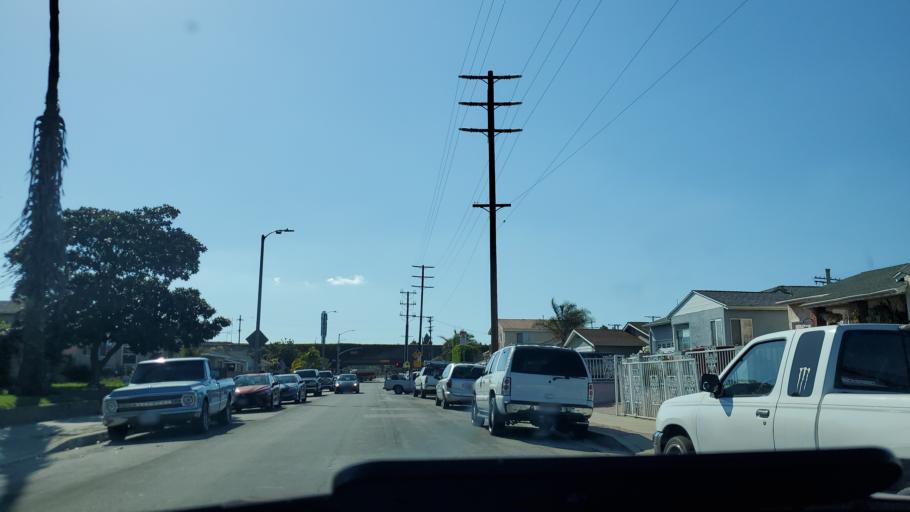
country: US
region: California
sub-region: Los Angeles County
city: Lomita
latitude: 33.7860
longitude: -118.2791
